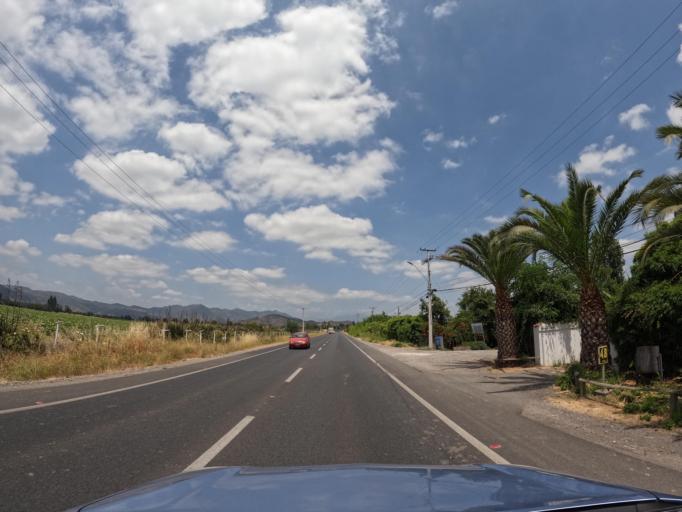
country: CL
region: Maule
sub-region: Provincia de Curico
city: Curico
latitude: -35.0243
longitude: -71.2007
